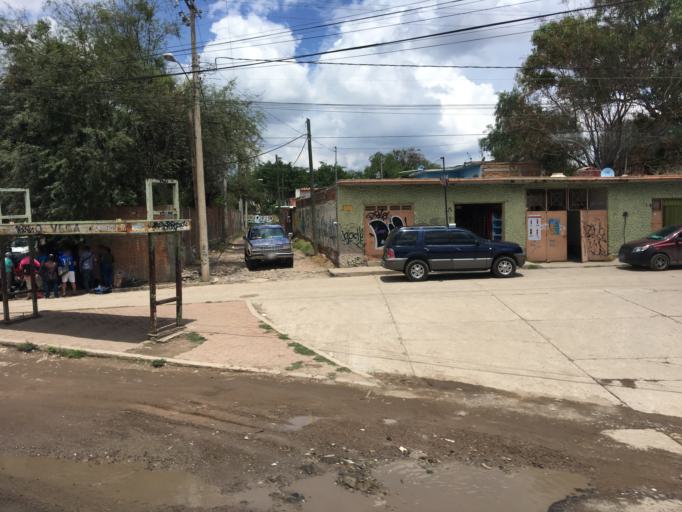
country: MX
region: Guanajuato
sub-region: Irapuato
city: Ex-Hacienda del Copal
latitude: 20.7269
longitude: -101.3442
